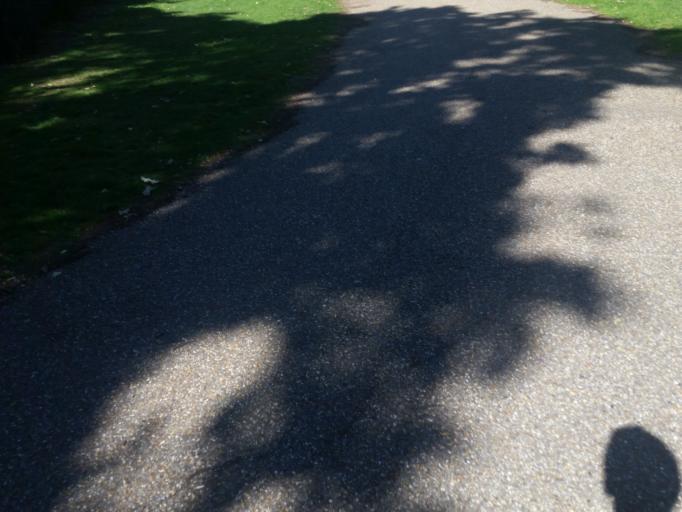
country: GB
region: England
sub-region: Greater London
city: Harringay
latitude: 51.5704
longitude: -0.0984
